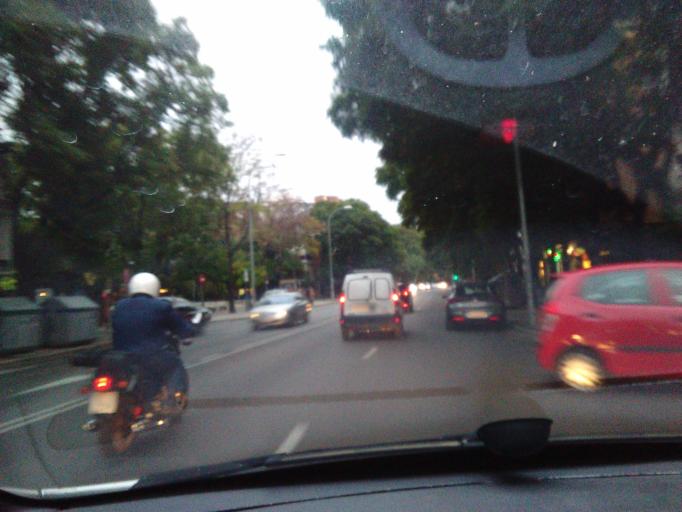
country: ES
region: Andalusia
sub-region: Provincia de Sevilla
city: Sevilla
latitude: 37.3745
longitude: -5.9676
